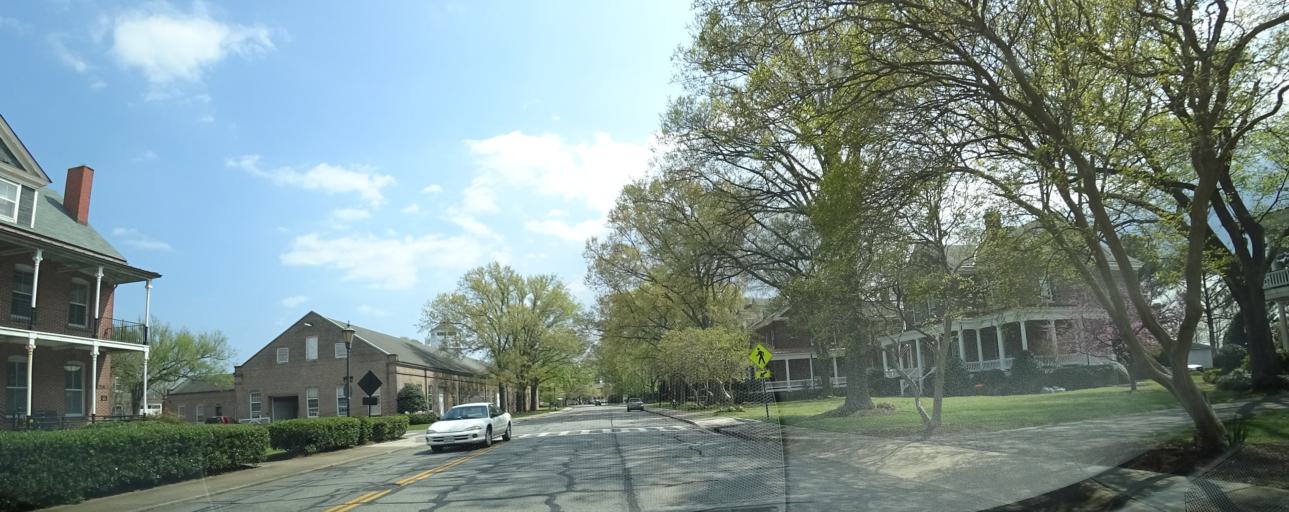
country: US
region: Virginia
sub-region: City of Hampton
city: East Hampton
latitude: 37.0062
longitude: -76.3125
